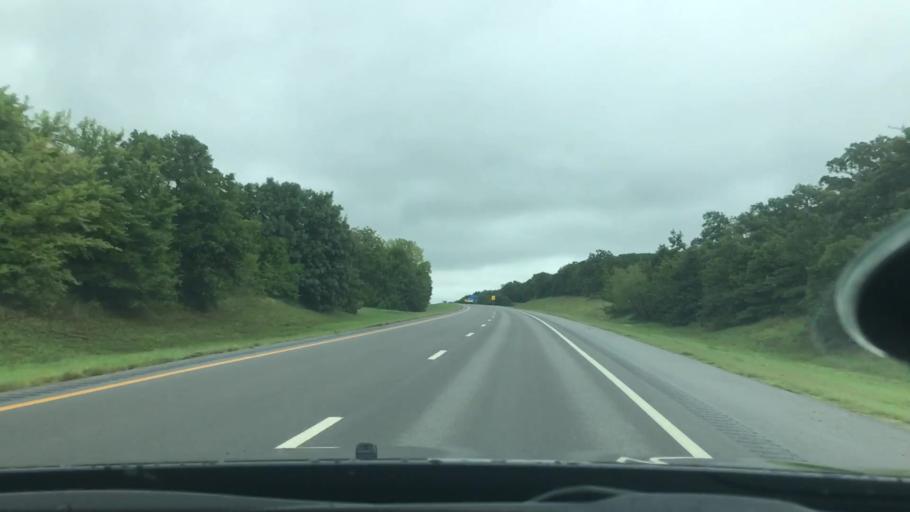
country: US
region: Oklahoma
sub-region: Okmulgee County
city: Morris
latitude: 35.4347
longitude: -95.7943
